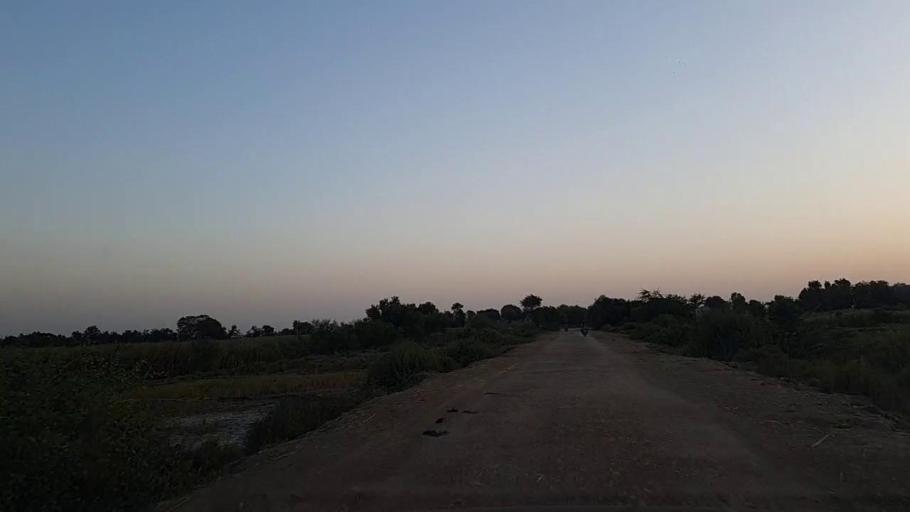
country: PK
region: Sindh
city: Mirpur Batoro
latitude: 24.6194
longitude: 68.1839
